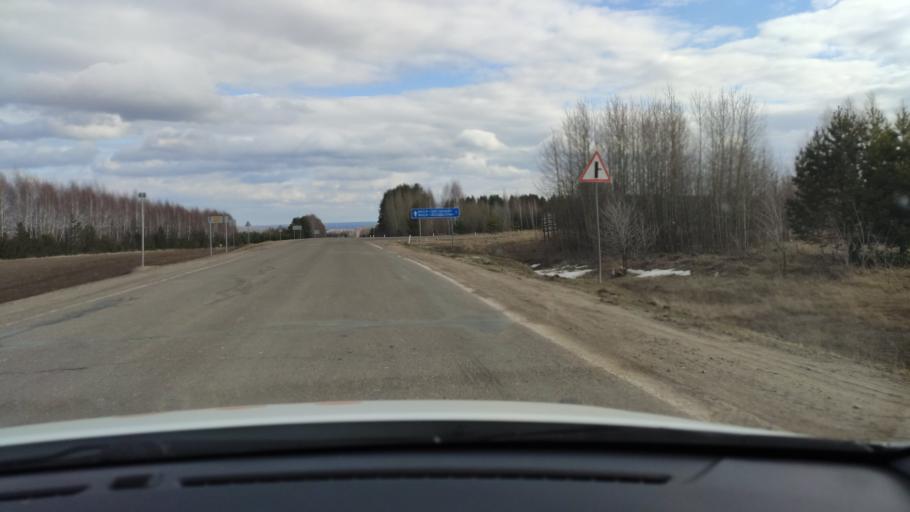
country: RU
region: Tatarstan
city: Vysokaya Gora
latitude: 56.0398
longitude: 49.2195
